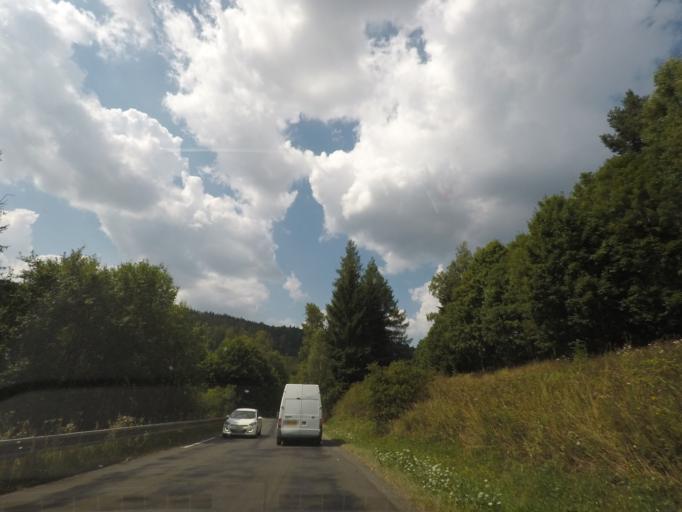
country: CZ
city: Radvanice
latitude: 50.5989
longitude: 16.0198
